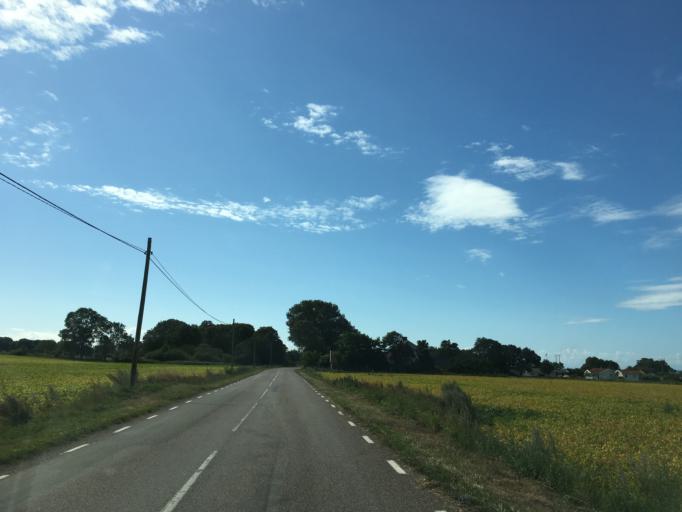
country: SE
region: Kalmar
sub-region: Morbylanga Kommun
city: Moerbylanga
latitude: 56.4201
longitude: 16.4134
